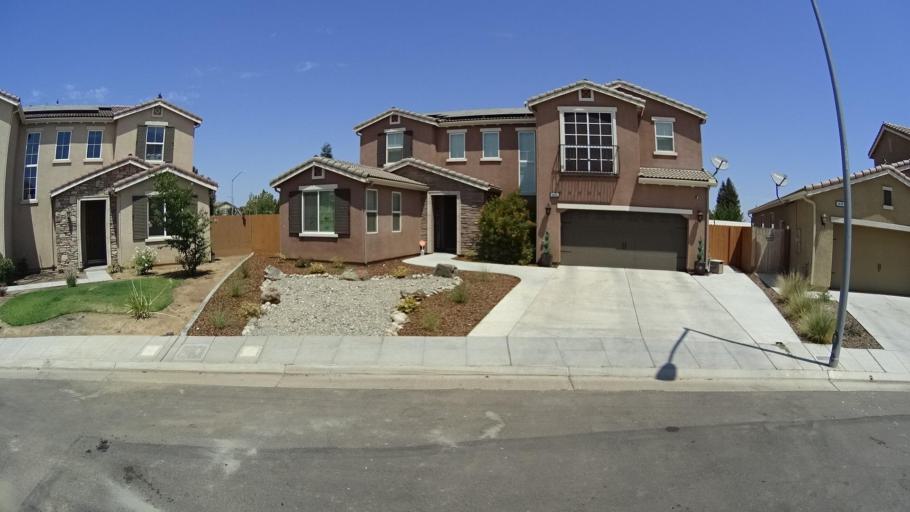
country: US
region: California
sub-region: Fresno County
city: Tarpey Village
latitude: 36.7858
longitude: -119.6544
